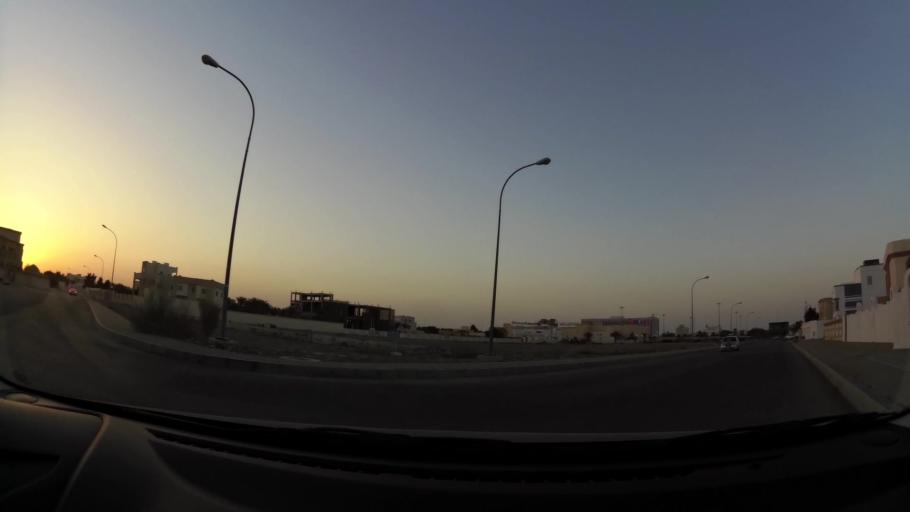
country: OM
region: Muhafazat Masqat
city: As Sib al Jadidah
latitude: 23.6458
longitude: 58.2134
